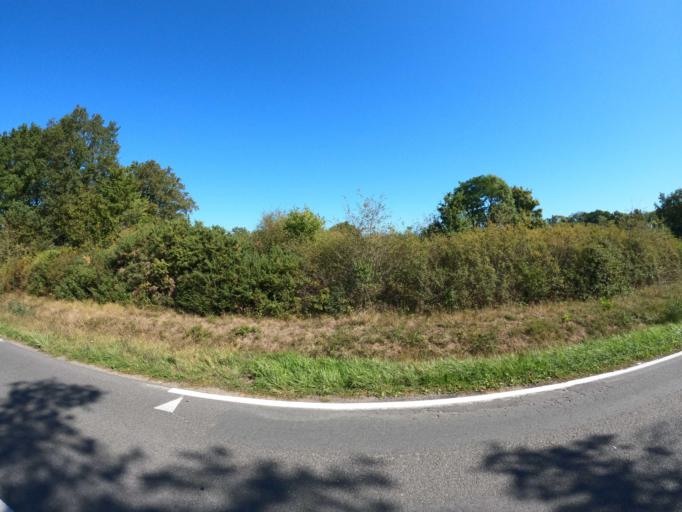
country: FR
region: Poitou-Charentes
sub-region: Departement de la Vienne
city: Lathus-Saint-Remy
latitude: 46.3060
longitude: 0.9845
